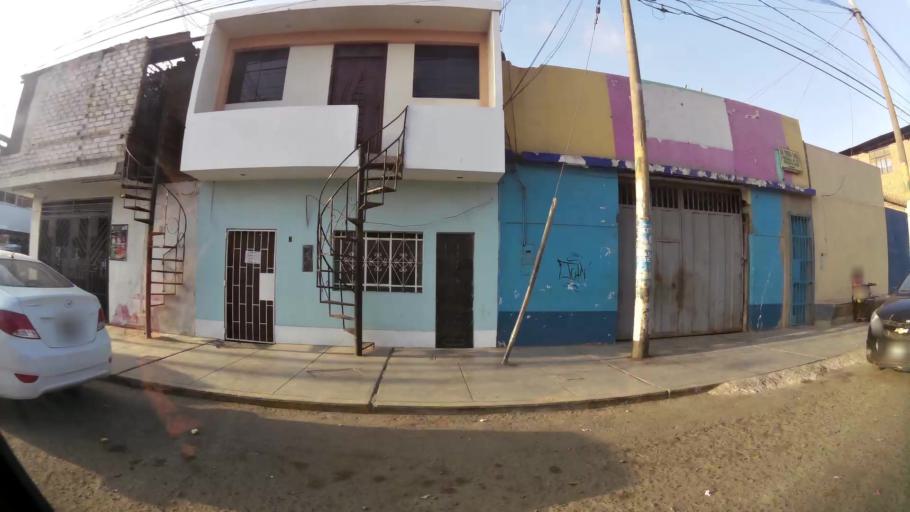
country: PE
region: La Libertad
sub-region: Provincia de Trujillo
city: El Porvenir
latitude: -8.0878
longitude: -78.9985
